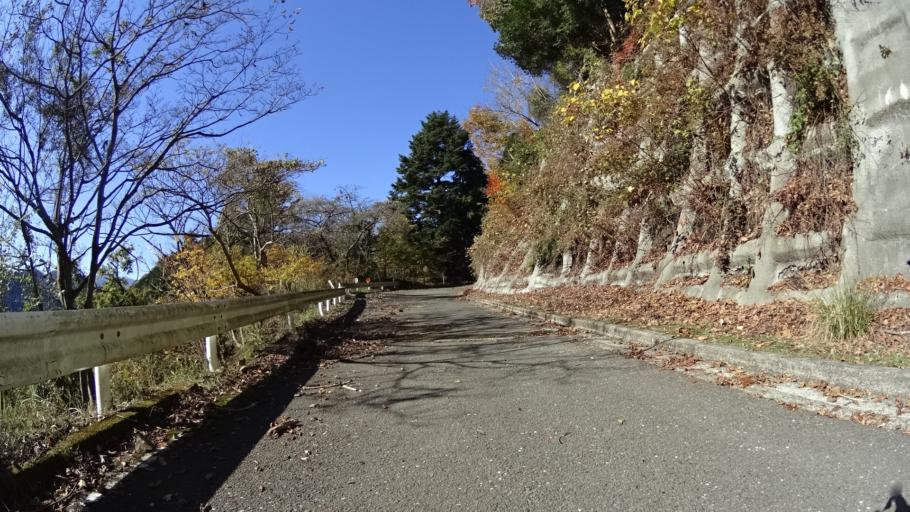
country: JP
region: Kanagawa
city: Atsugi
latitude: 35.5032
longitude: 139.2760
